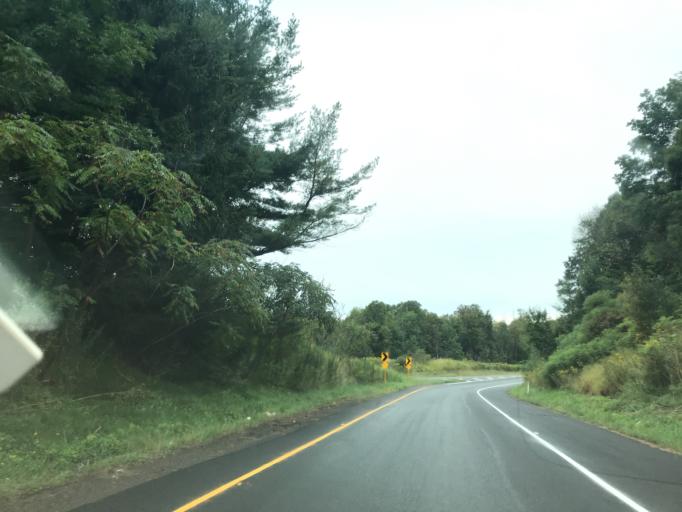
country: US
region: Pennsylvania
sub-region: Lackawanna County
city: Chinchilla
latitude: 41.4831
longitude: -75.6786
